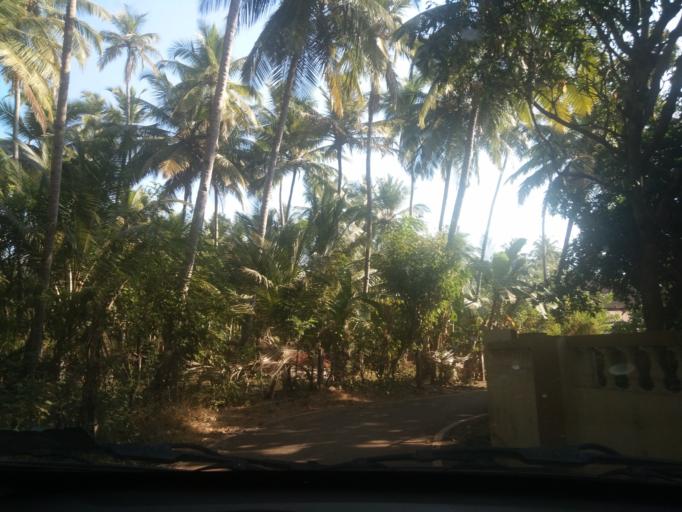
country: IN
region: Goa
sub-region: South Goa
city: Sancoale
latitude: 15.3523
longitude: 73.8901
